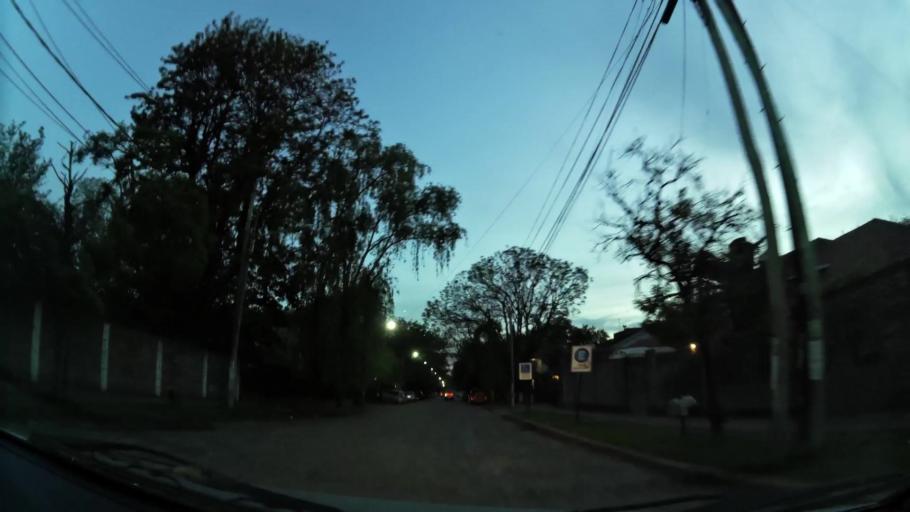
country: AR
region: Buenos Aires
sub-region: Partido de Quilmes
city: Quilmes
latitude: -34.8063
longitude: -58.2800
